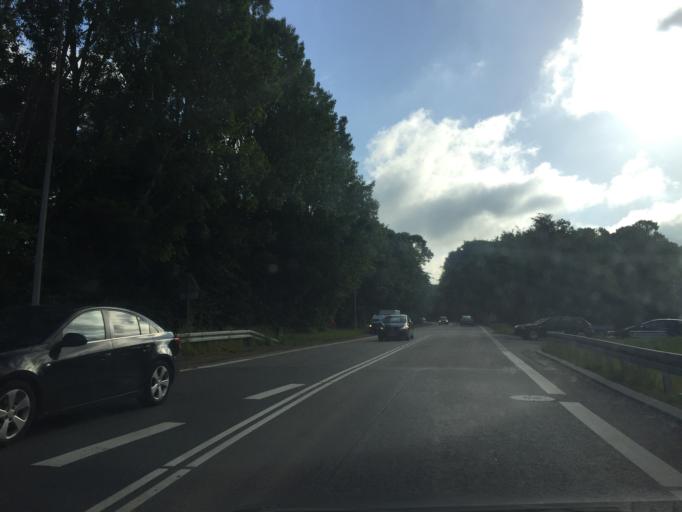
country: DK
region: Zealand
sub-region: Slagelse Kommune
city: Slagelse
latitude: 55.3909
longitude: 11.3599
